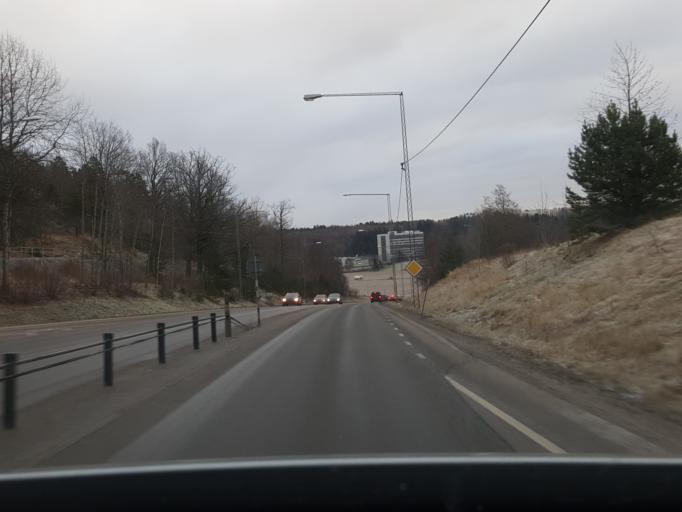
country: SE
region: Stockholm
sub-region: Botkyrka Kommun
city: Tumba
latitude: 59.2089
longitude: 17.8362
